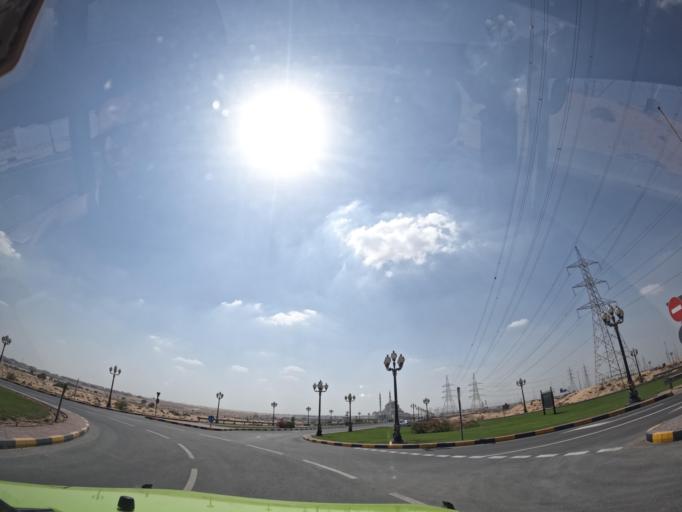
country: AE
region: Ash Shariqah
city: Sharjah
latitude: 25.2482
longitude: 55.5725
